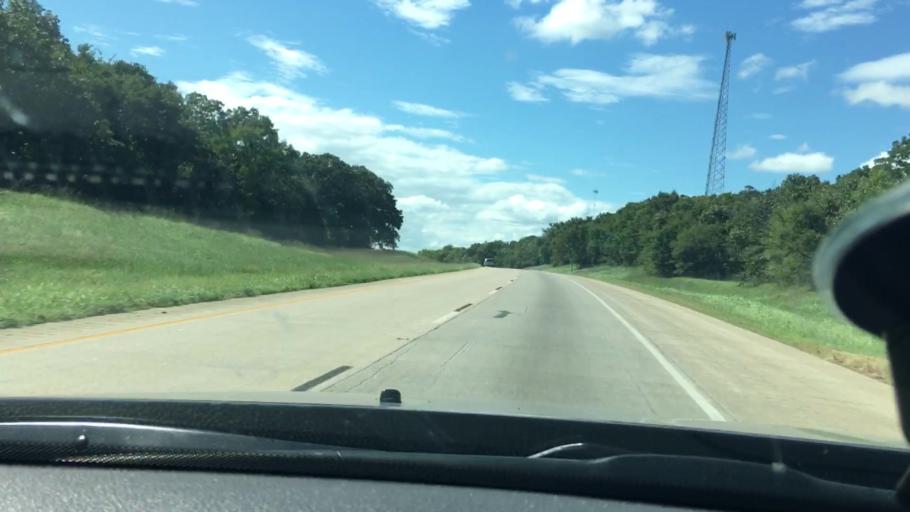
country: US
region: Oklahoma
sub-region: Sequoyah County
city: Vian
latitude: 35.4919
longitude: -94.9999
